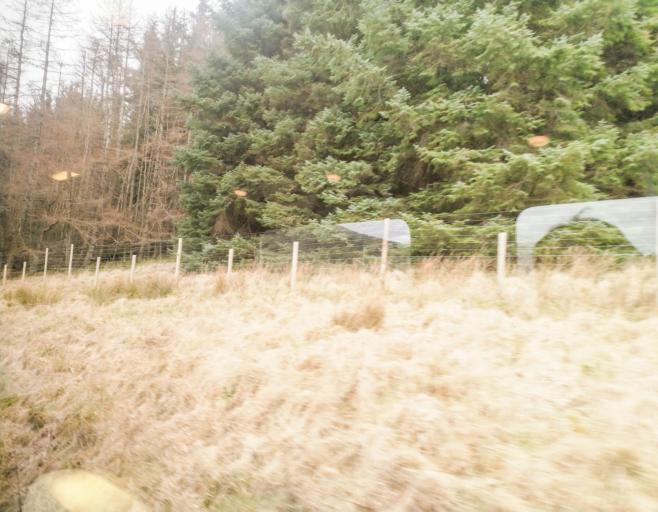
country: GB
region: Scotland
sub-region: Argyll and Bute
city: Garelochhead
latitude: 56.4398
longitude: -4.7070
